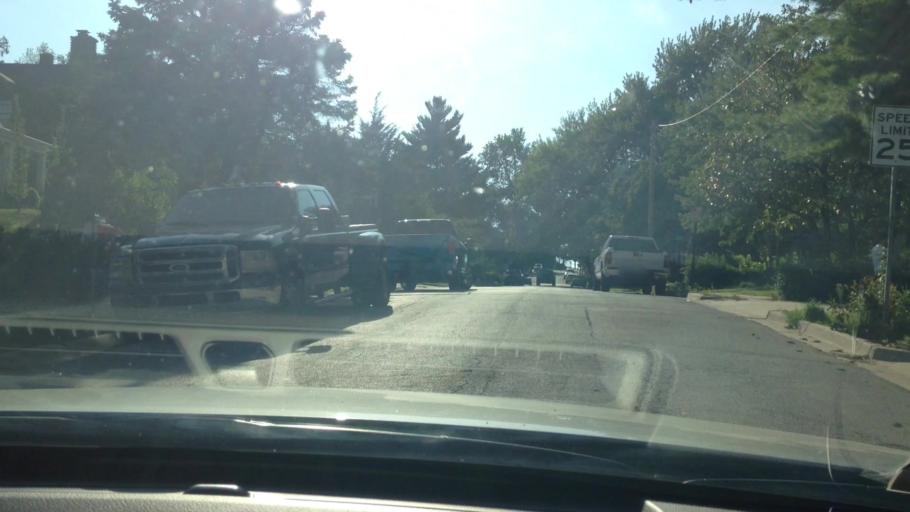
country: US
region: Kansas
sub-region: Johnson County
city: Westwood
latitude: 39.0334
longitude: -94.5845
